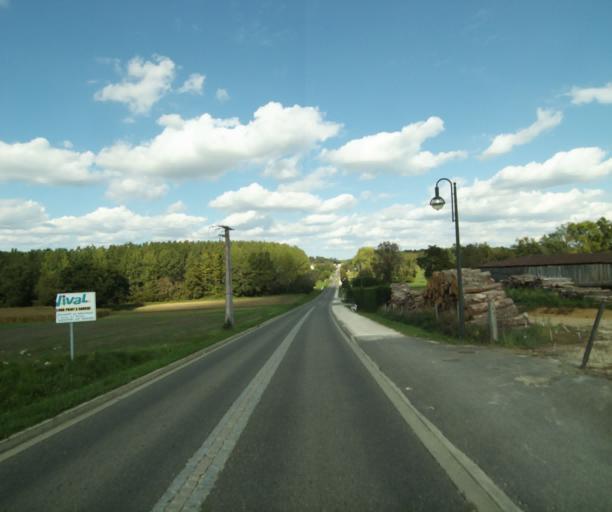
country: FR
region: Midi-Pyrenees
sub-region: Departement du Gers
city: Cazaubon
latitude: 43.9399
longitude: -0.0565
